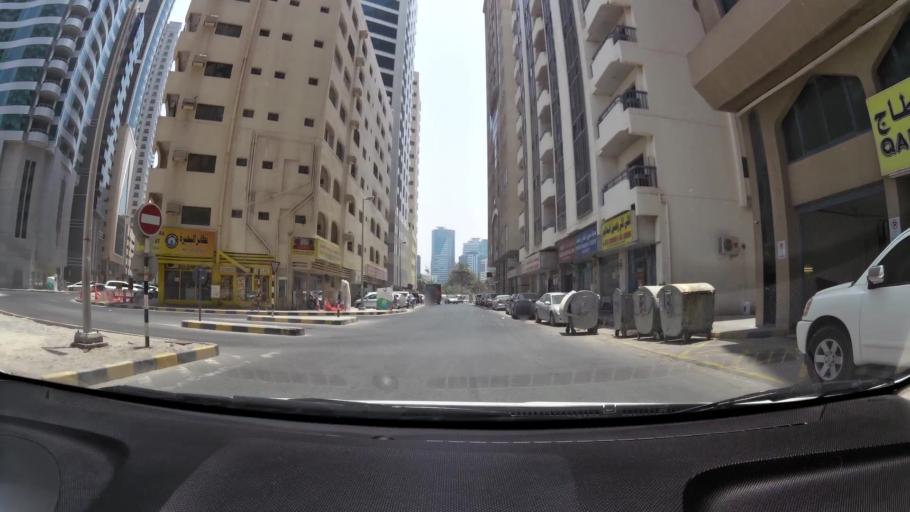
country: AE
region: Ash Shariqah
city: Sharjah
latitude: 25.3360
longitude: 55.3752
